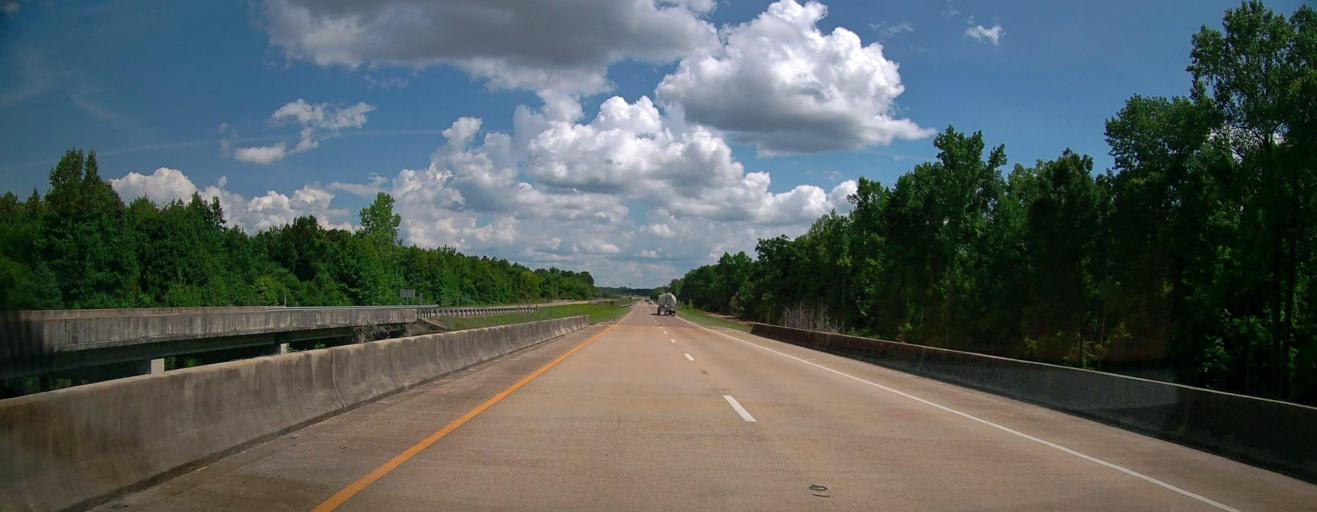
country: US
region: Mississippi
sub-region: Lowndes County
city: Columbus Air Force Base
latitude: 33.6729
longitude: -88.4288
